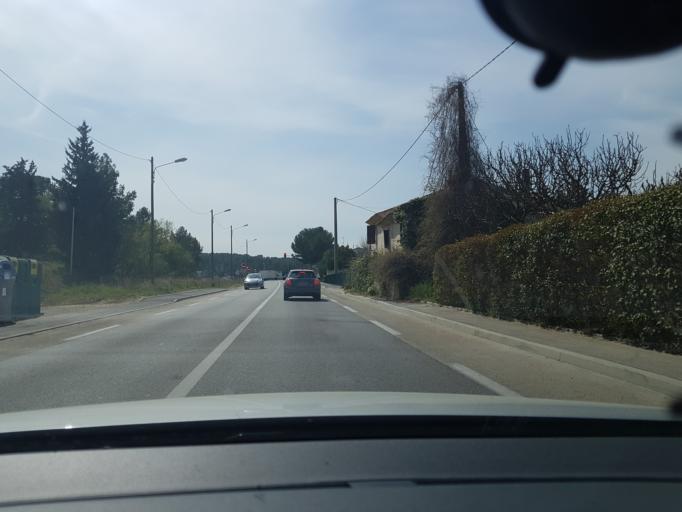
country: FR
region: Provence-Alpes-Cote d'Azur
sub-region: Departement des Bouches-du-Rhone
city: Bouc-Bel-Air
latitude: 43.4728
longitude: 5.4095
